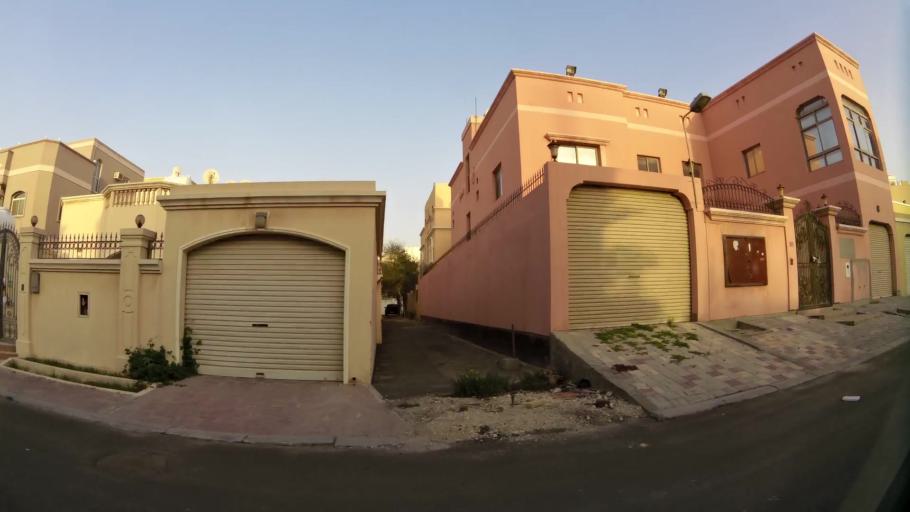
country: BH
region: Northern
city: Madinat `Isa
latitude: 26.1881
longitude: 50.4770
